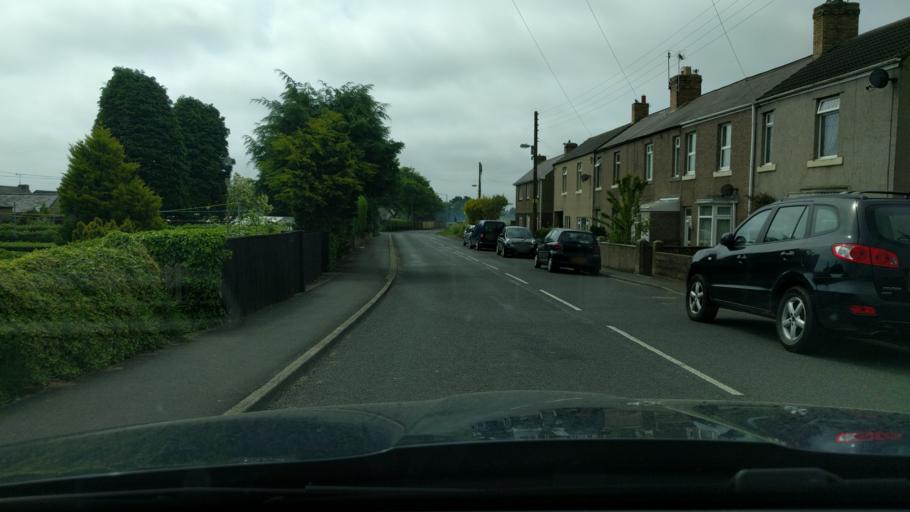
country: GB
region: England
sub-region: Northumberland
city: Acklington
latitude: 55.3035
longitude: -1.6137
